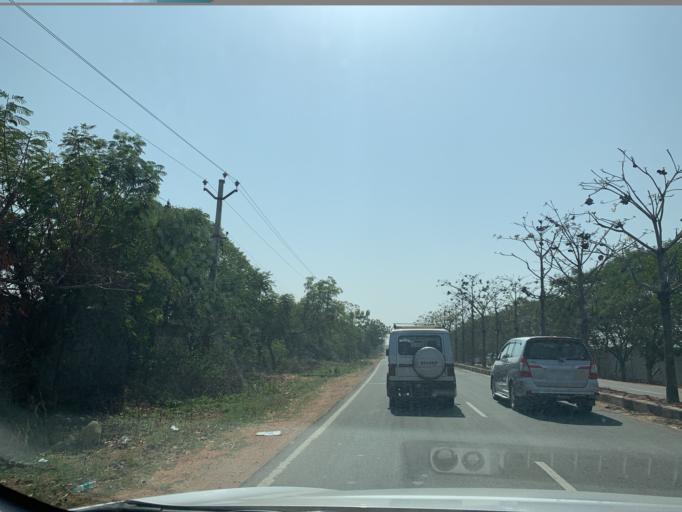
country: IN
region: Telangana
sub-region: Rangareddi
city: Sriramnagar
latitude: 17.3377
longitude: 78.3045
